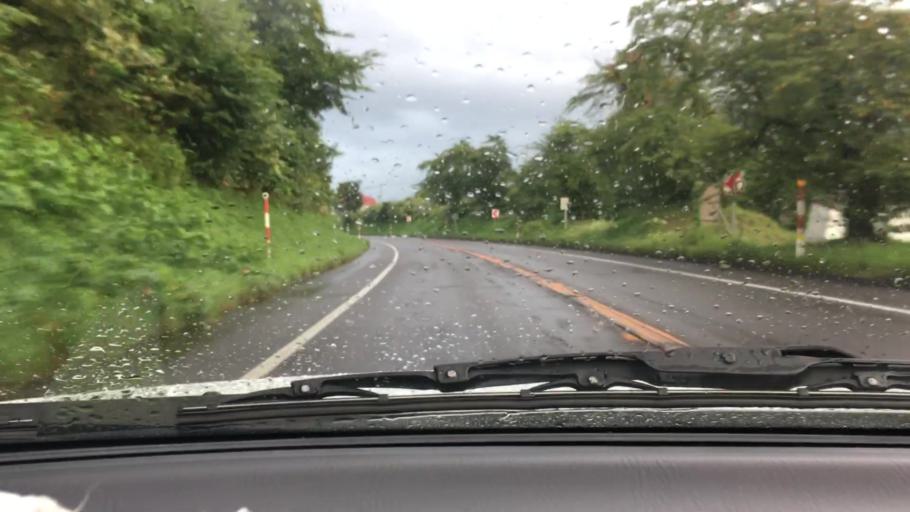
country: JP
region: Hokkaido
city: Nanae
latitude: 42.0828
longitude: 140.5867
